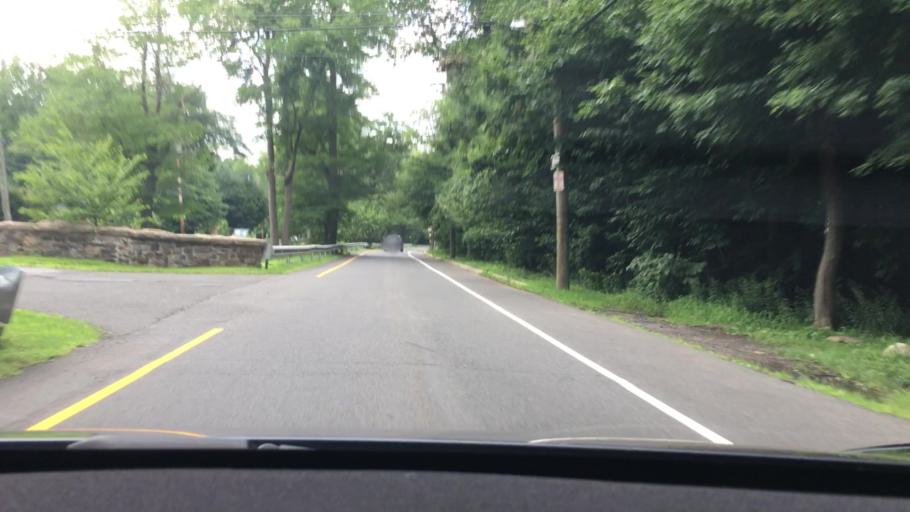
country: US
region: New York
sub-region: Westchester County
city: New Rochelle
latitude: 40.9400
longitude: -73.7786
